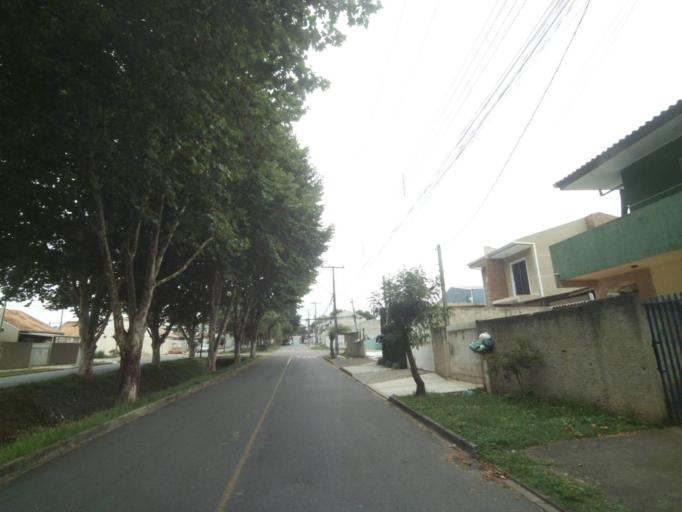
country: BR
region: Parana
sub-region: Araucaria
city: Araucaria
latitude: -25.5507
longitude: -49.3395
